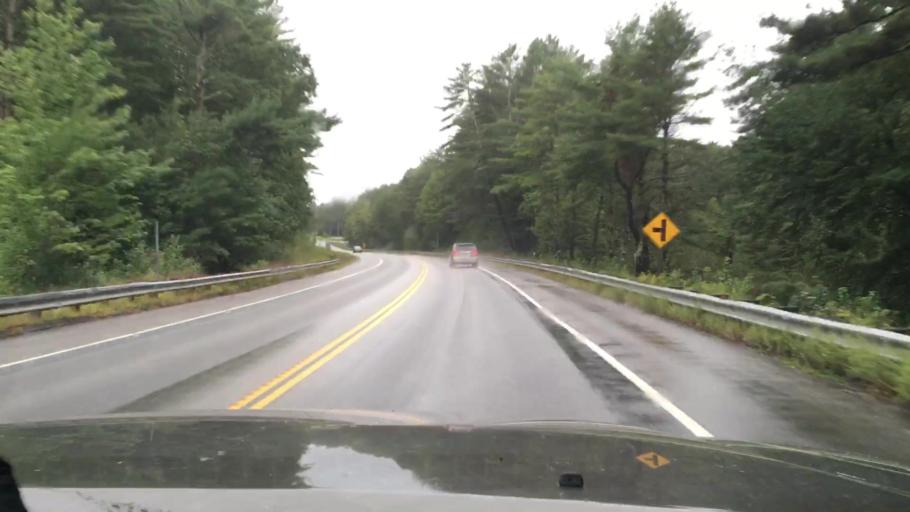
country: US
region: New Hampshire
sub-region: Cheshire County
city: Westmoreland
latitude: 42.9165
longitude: -72.3989
